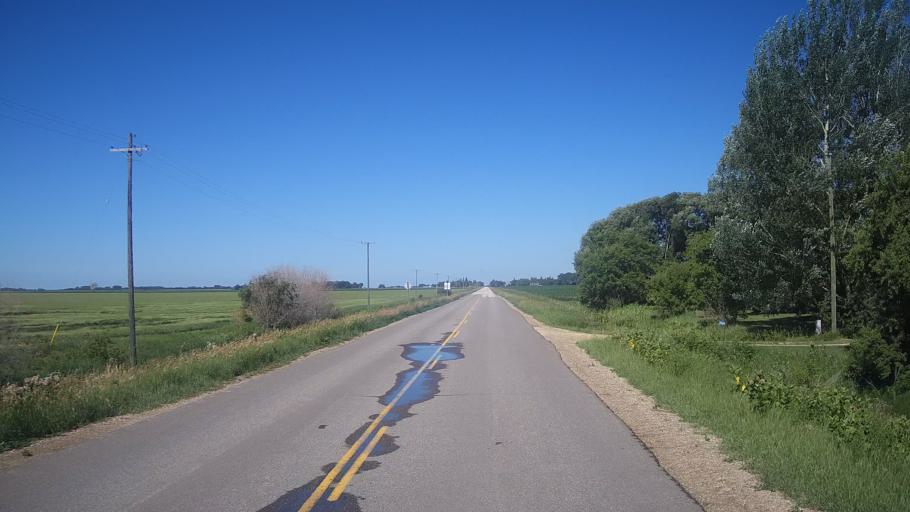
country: CA
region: Manitoba
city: Portage la Prairie
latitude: 50.0437
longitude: -98.0340
